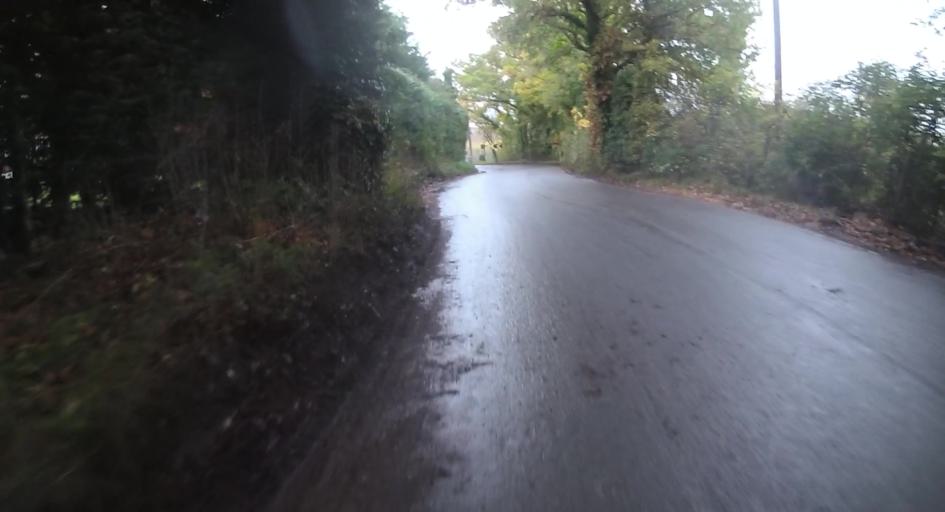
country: GB
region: England
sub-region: Surrey
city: Farnham
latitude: 51.2192
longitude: -0.8367
